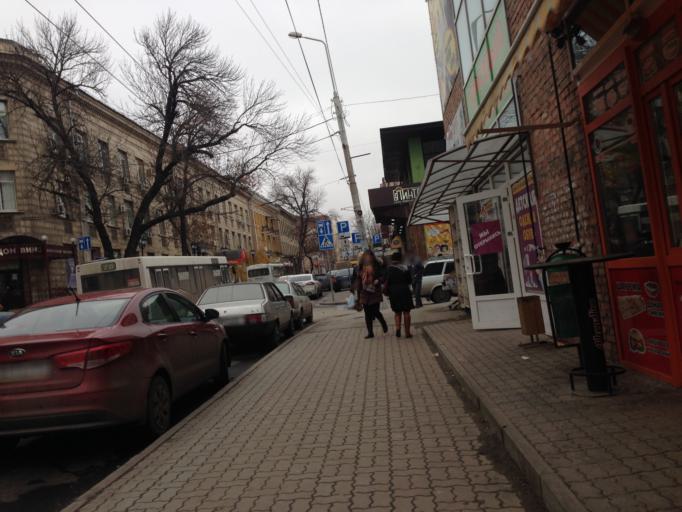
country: RU
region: Rostov
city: Rostov-na-Donu
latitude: 47.2185
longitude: 39.7142
